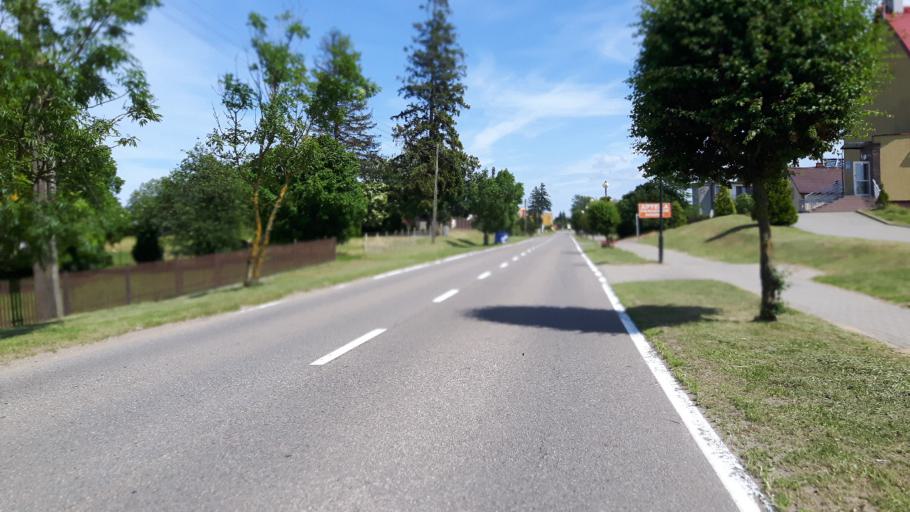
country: PL
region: Pomeranian Voivodeship
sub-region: Powiat wejherowski
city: Gniewino
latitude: 54.7166
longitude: 18.0212
